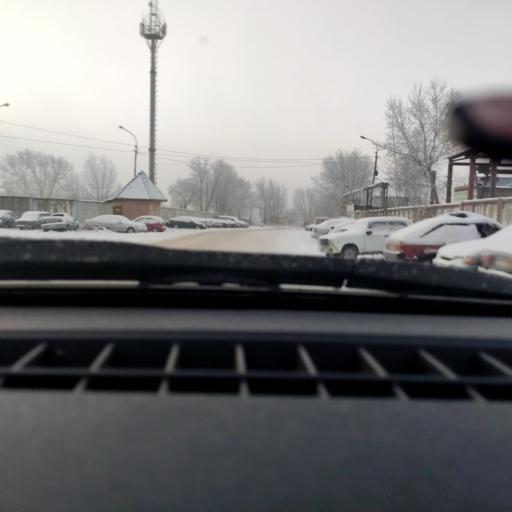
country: RU
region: Bashkortostan
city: Ufa
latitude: 54.8564
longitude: 56.0866
